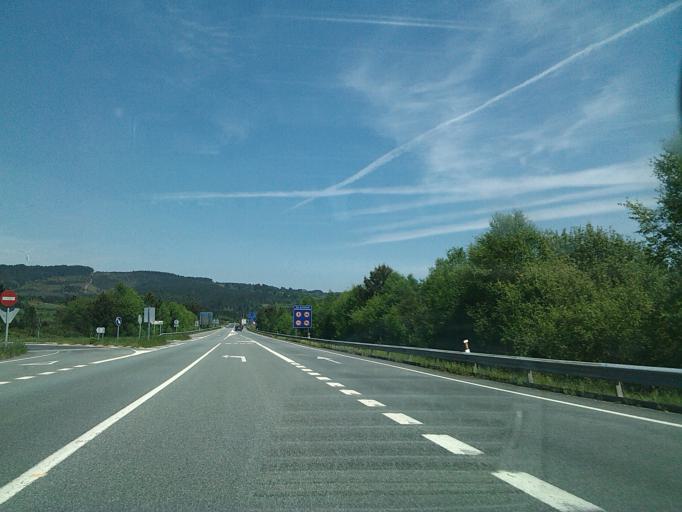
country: ES
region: Galicia
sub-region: Provincia de Lugo
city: Guitiriz
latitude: 43.1897
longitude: -7.9584
